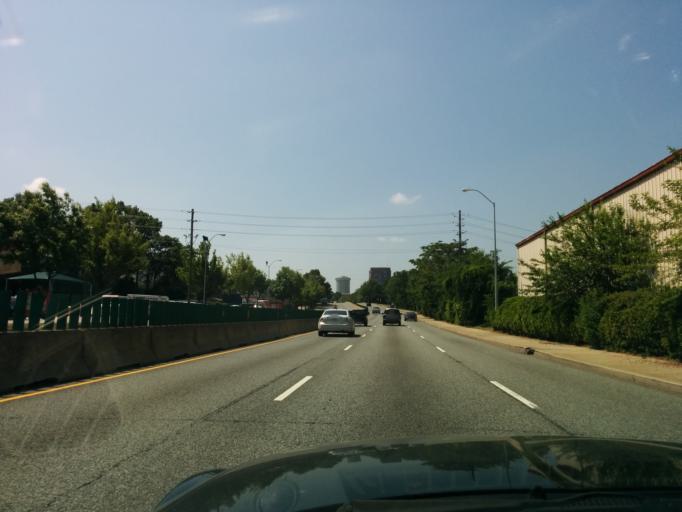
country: US
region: North Carolina
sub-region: Wake County
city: Raleigh
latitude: 35.7921
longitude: -78.6423
